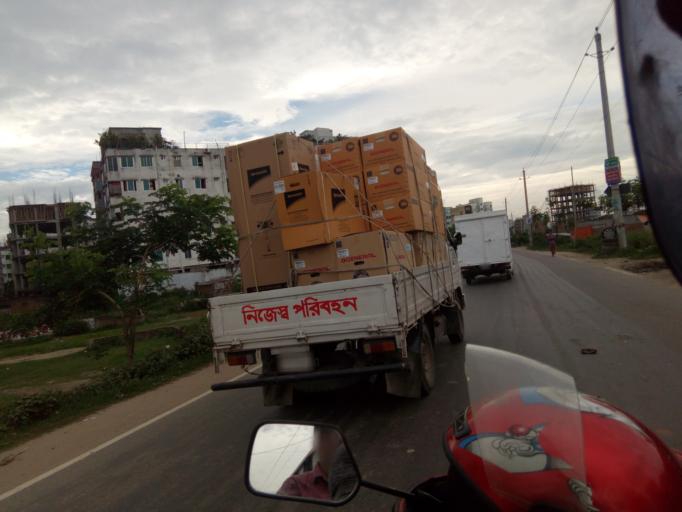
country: BD
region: Dhaka
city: Paltan
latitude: 23.7595
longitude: 90.4465
